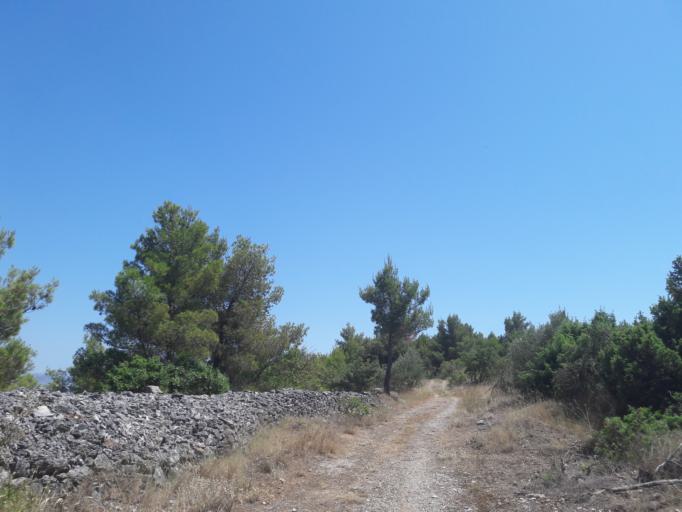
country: HR
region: Sibensko-Kniniska
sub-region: Grad Sibenik
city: Sibenik
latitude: 43.6921
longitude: 15.8546
